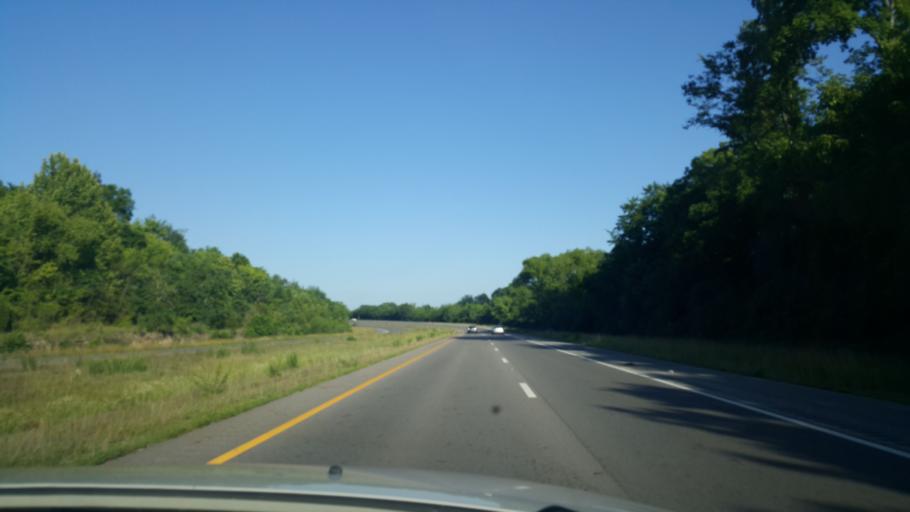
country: US
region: Tennessee
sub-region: Maury County
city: Columbia
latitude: 35.6300
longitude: -87.0969
